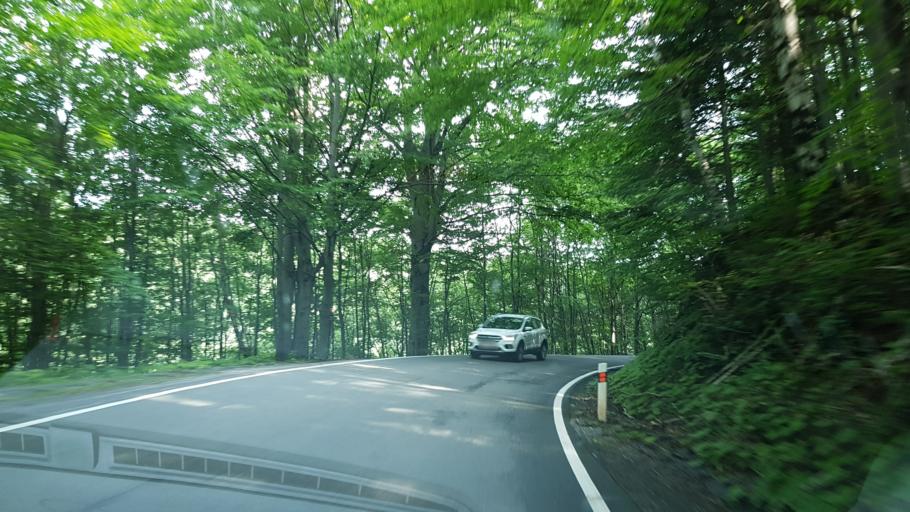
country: CZ
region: Olomoucky
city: Ceska Ves
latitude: 50.2191
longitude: 17.2542
